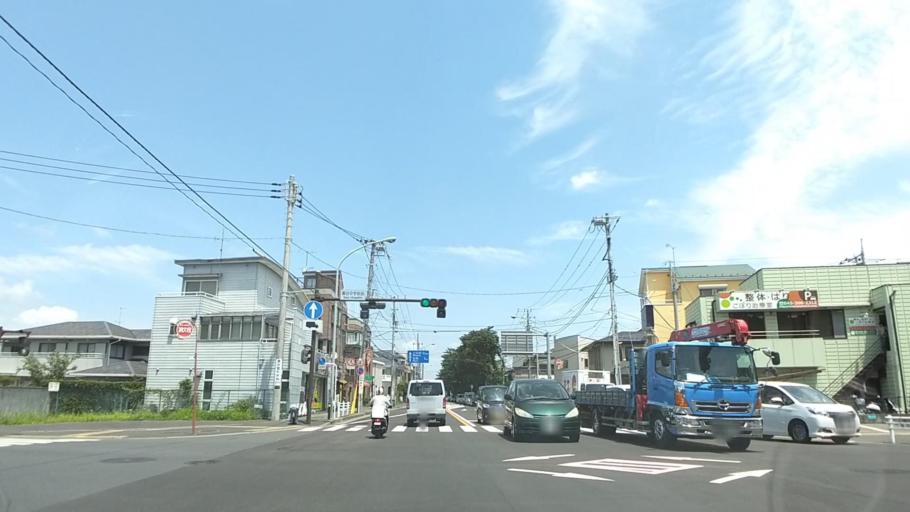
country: JP
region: Kanagawa
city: Minami-rinkan
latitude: 35.4723
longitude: 139.4807
